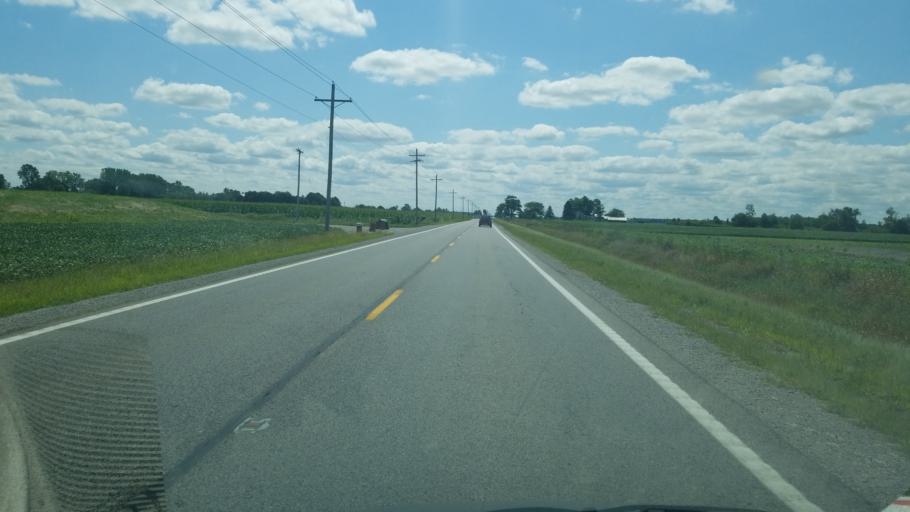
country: US
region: Ohio
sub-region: Fulton County
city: Delta
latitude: 41.6506
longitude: -84.0352
